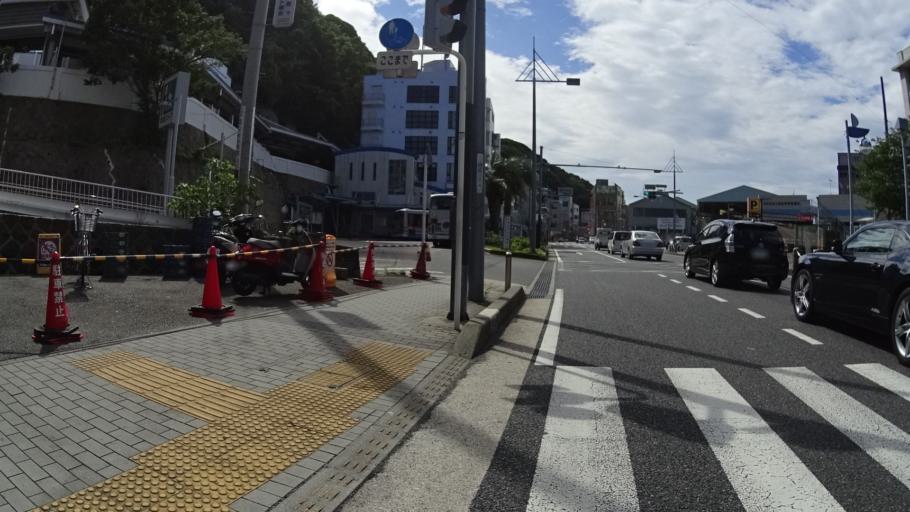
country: JP
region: Kanagawa
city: Yokosuka
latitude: 35.2509
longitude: 139.7146
